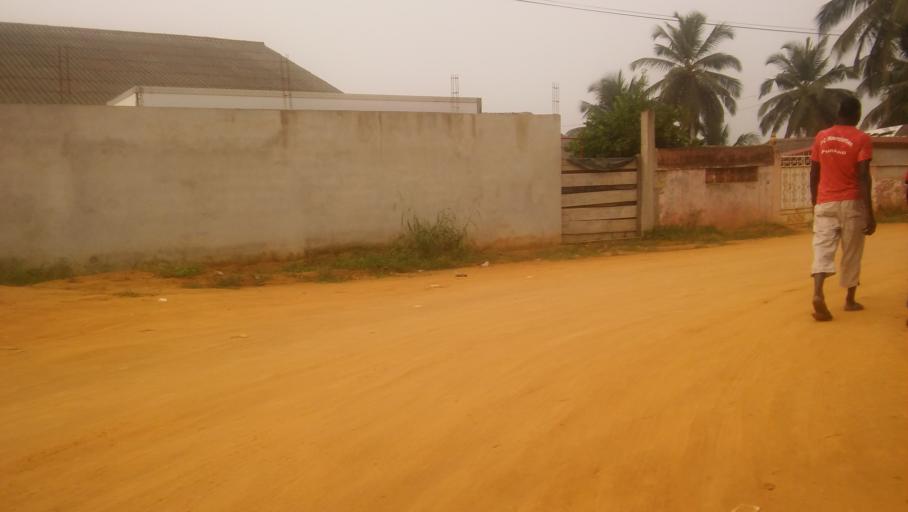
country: CI
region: Sud-Comoe
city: Grand-Bassam
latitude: 5.1998
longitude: -3.7349
